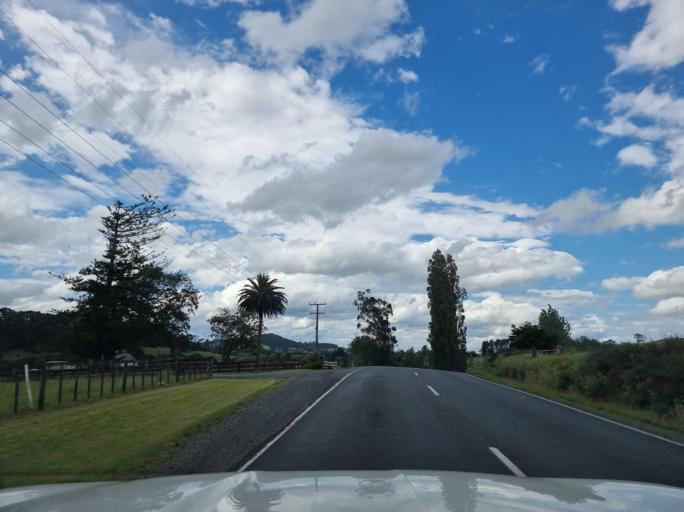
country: NZ
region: Northland
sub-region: Whangarei
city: Maungatapere
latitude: -35.8573
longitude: 174.2528
